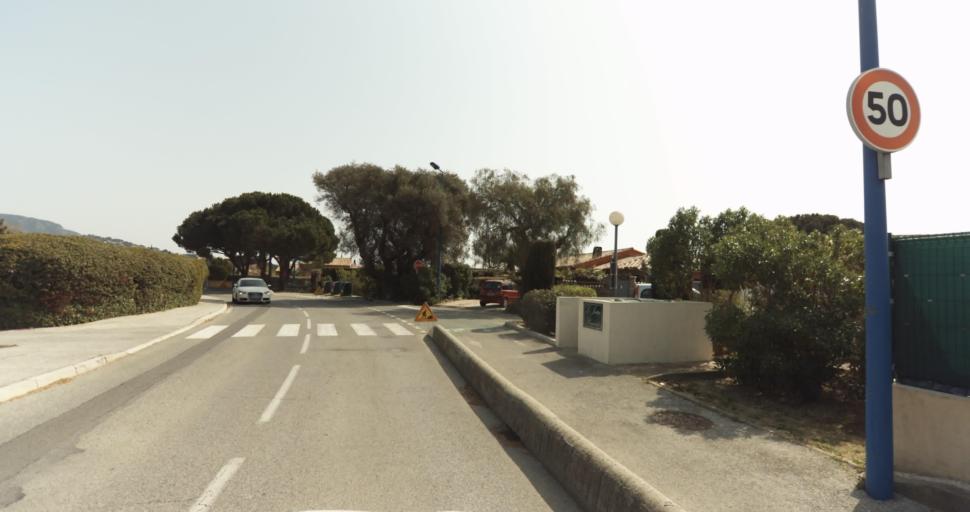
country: FR
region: Provence-Alpes-Cote d'Azur
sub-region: Departement du Var
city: Bormes-les-Mimosas
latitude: 43.1357
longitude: 6.3424
